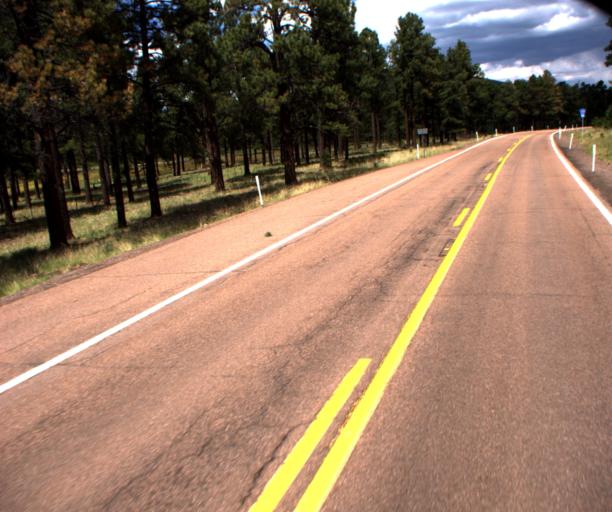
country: US
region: Arizona
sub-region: Apache County
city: Eagar
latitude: 34.0748
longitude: -109.4782
